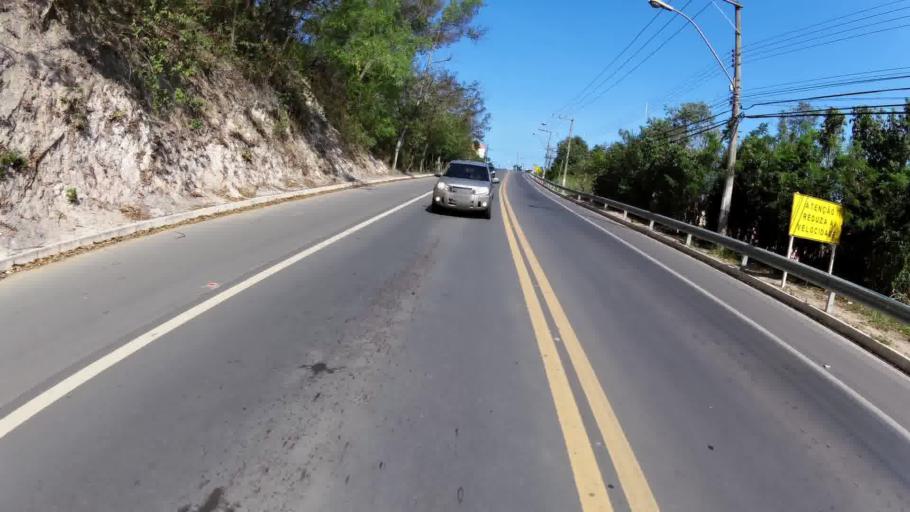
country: BR
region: Espirito Santo
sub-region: Piuma
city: Piuma
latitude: -20.8182
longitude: -40.6283
